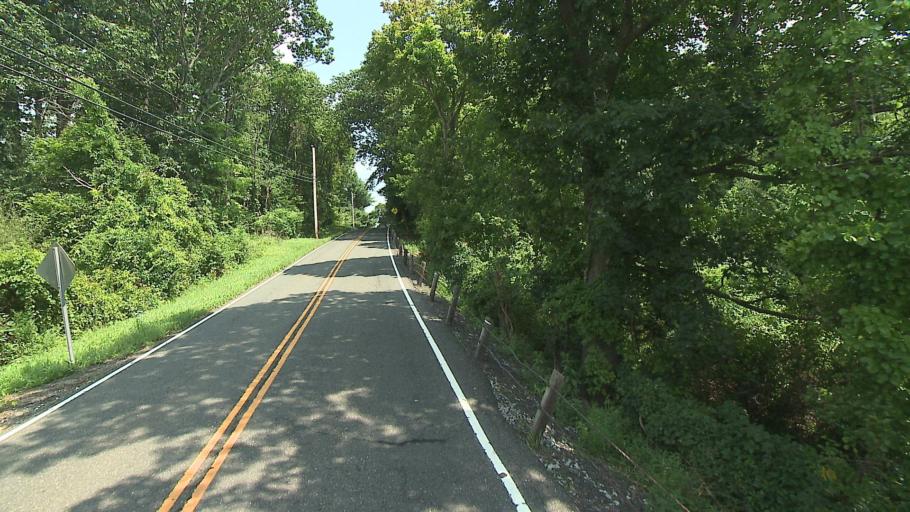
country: US
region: Connecticut
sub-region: Litchfield County
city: New Preston
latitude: 41.6310
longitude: -73.3624
